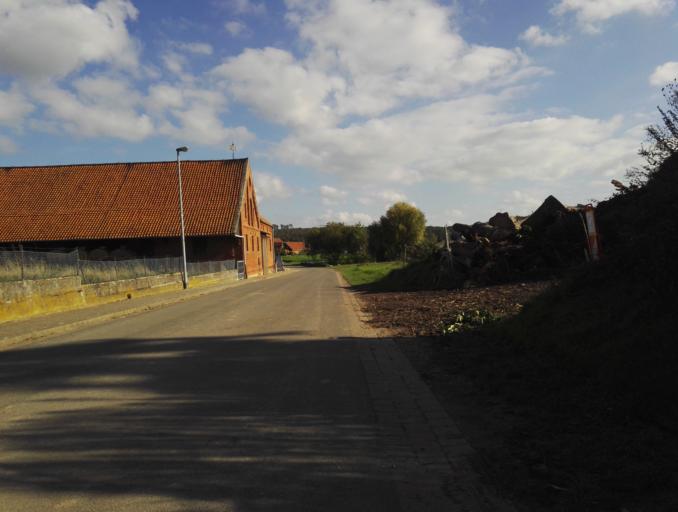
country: DE
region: Lower Saxony
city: Schellerten
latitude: 52.1444
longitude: 10.1275
